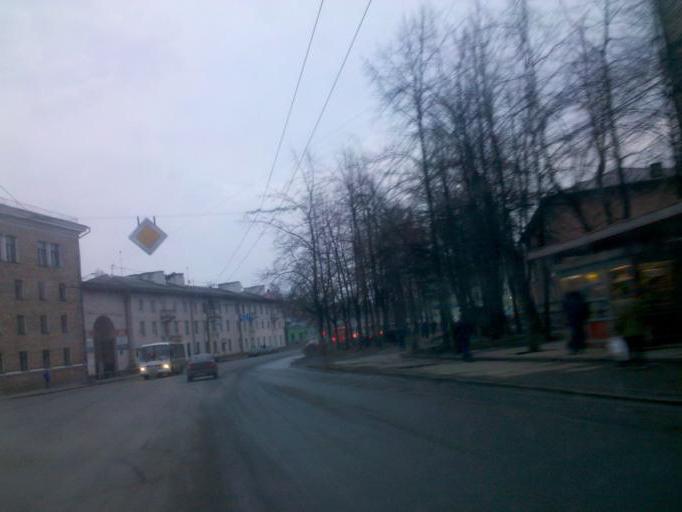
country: RU
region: Republic of Karelia
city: Petrozavodsk
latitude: 61.7830
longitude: 34.3841
